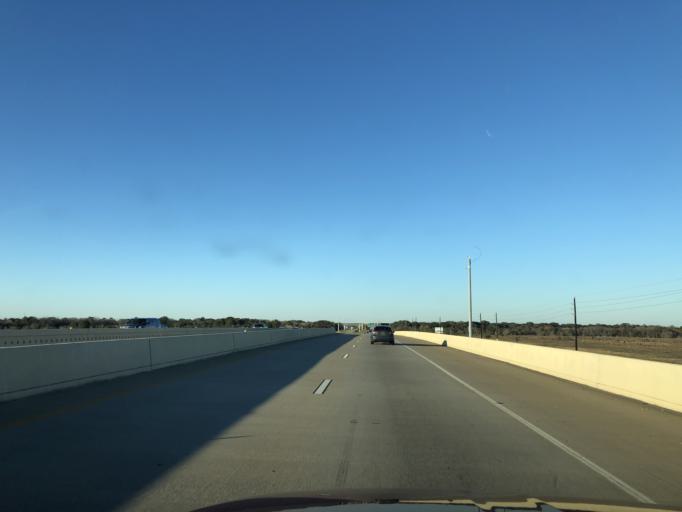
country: US
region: Texas
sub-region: Harris County
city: Cypress
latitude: 29.9529
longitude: -95.7696
